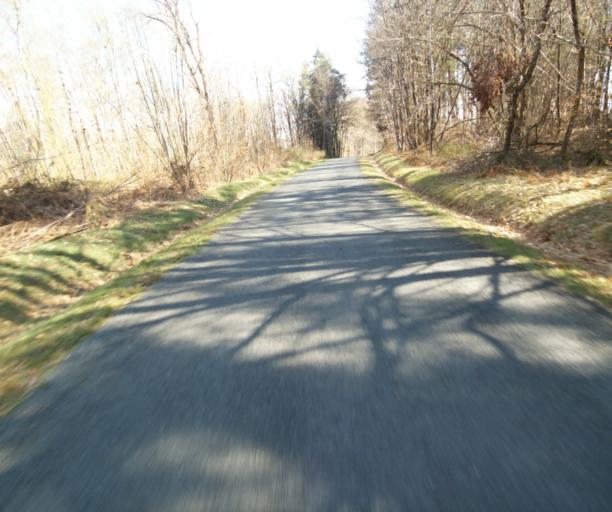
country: FR
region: Limousin
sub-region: Departement de la Correze
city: Correze
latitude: 45.2467
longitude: 1.9206
